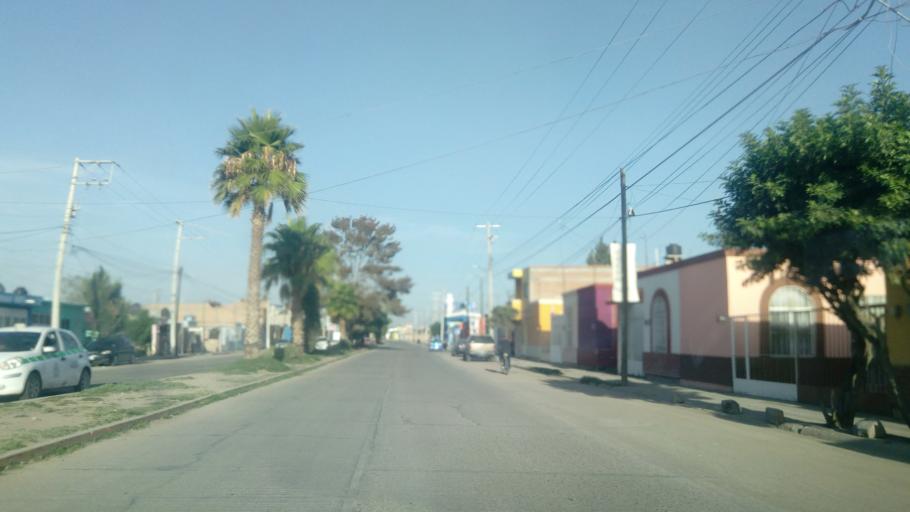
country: MX
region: Durango
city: Victoria de Durango
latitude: 24.0575
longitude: -104.5848
